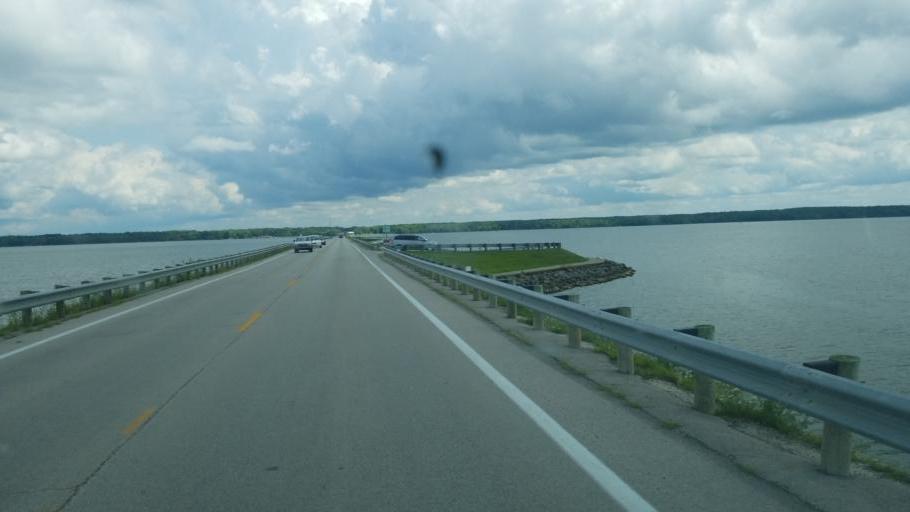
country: US
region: Ohio
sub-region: Ashtabula County
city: Andover
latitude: 41.6070
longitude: -80.5315
